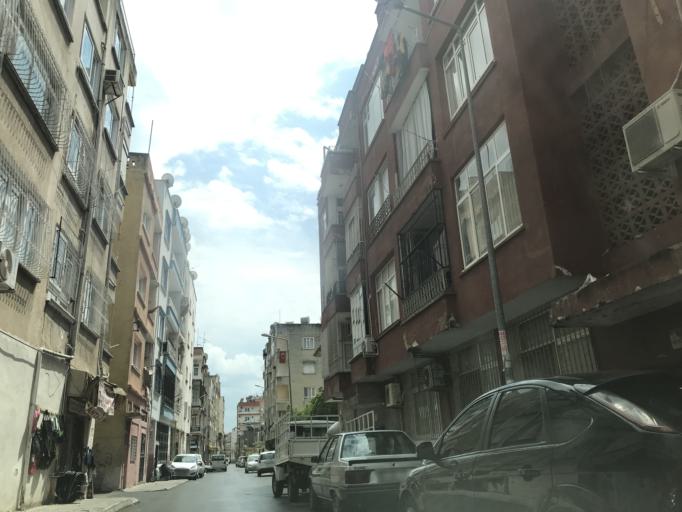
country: TR
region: Mersin
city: Mercin
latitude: 36.8048
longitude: 34.6274
